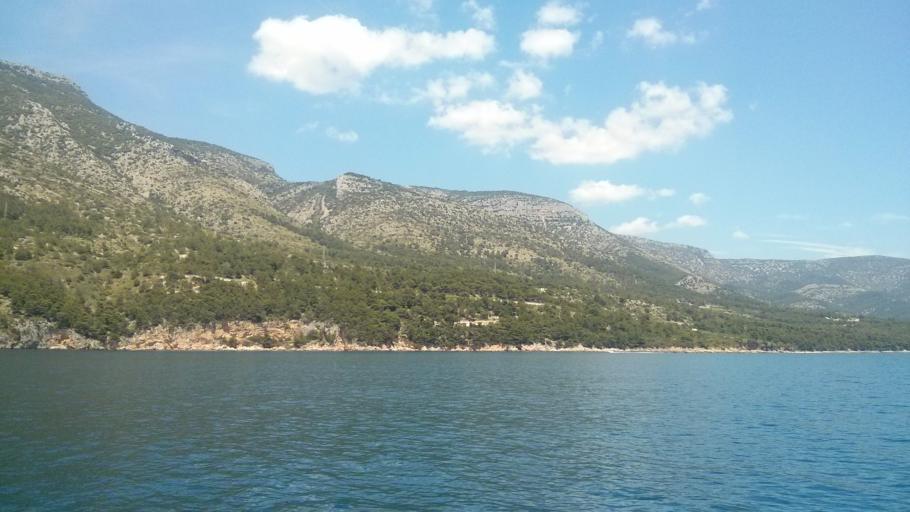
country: HR
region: Splitsko-Dalmatinska
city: Bol
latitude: 43.2570
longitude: 16.6102
